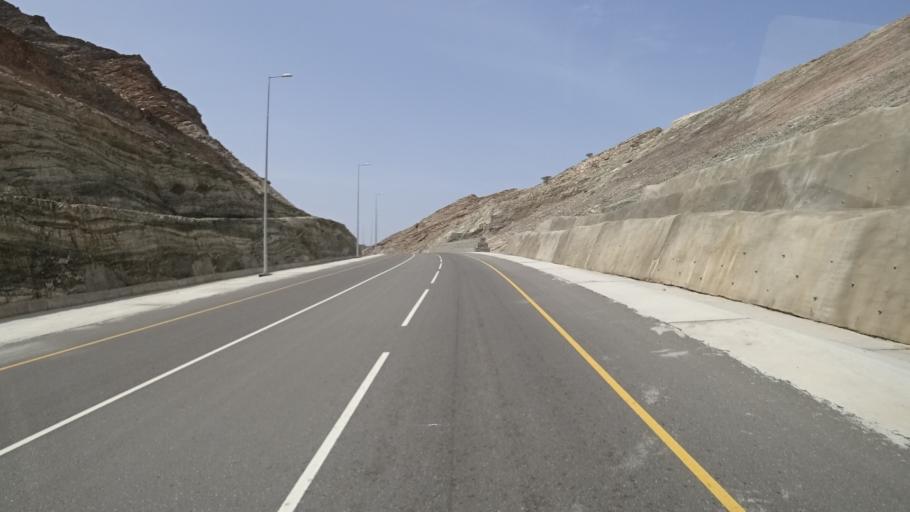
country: OM
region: Muhafazat Masqat
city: Muscat
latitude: 23.4435
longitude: 58.7582
